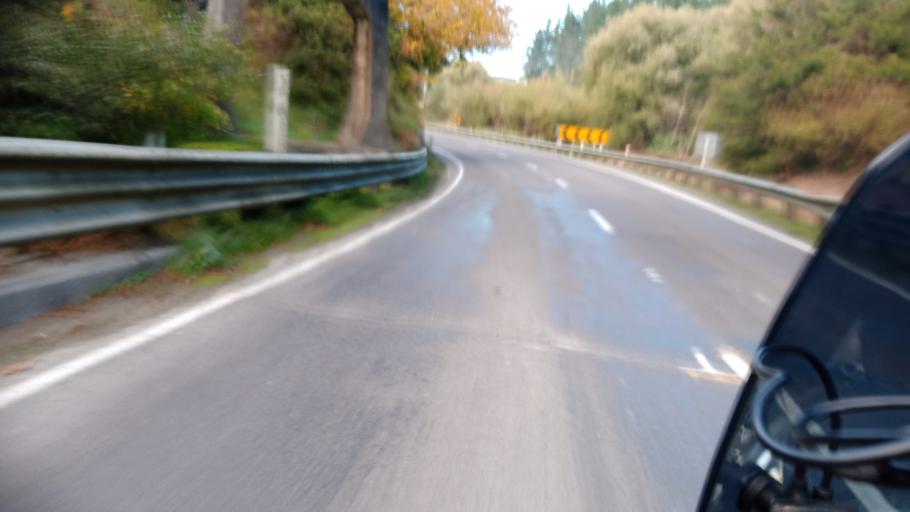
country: NZ
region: Gisborne
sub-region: Gisborne District
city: Gisborne
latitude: -38.8389
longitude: 177.8972
